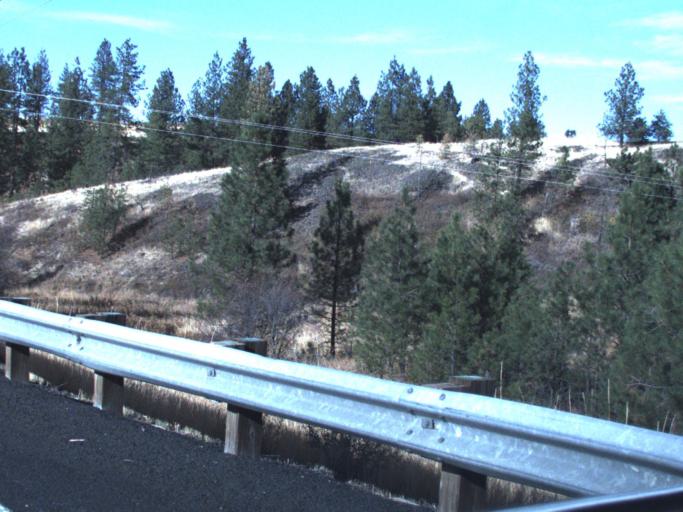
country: US
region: Washington
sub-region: Lincoln County
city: Davenport
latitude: 47.8633
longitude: -118.2467
